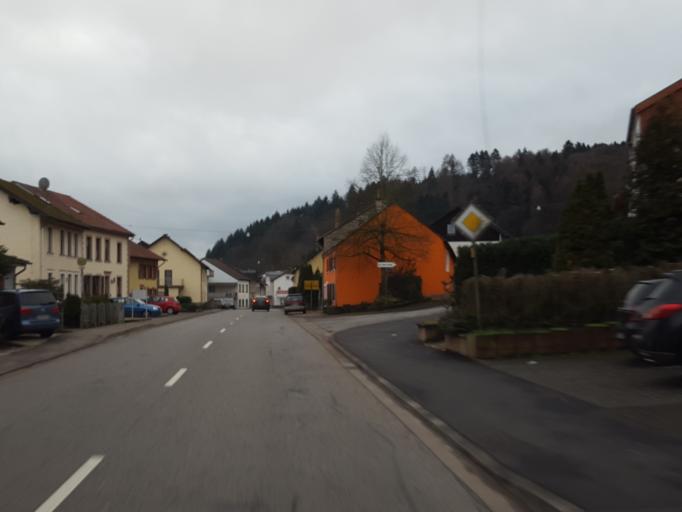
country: DE
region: Saarland
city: Beckingen
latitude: 49.4303
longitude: 6.7324
